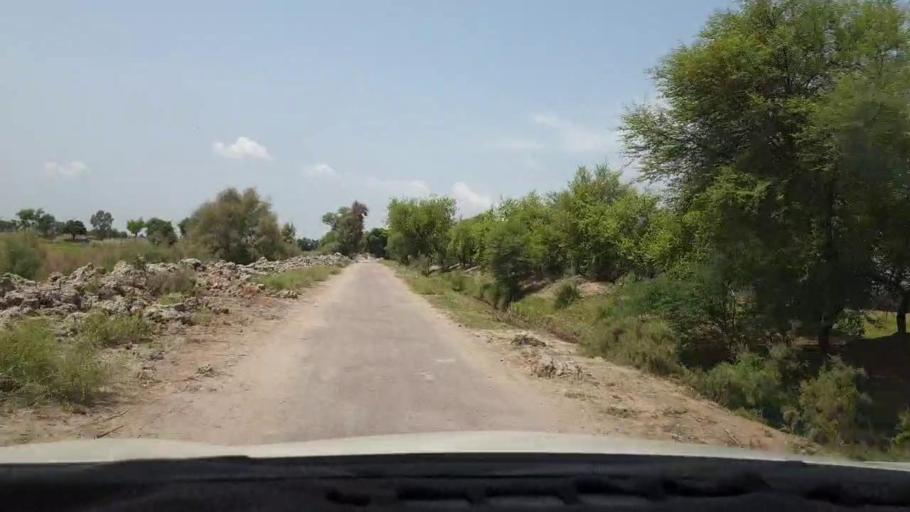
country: PK
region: Sindh
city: Ratodero
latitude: 27.8418
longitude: 68.2313
